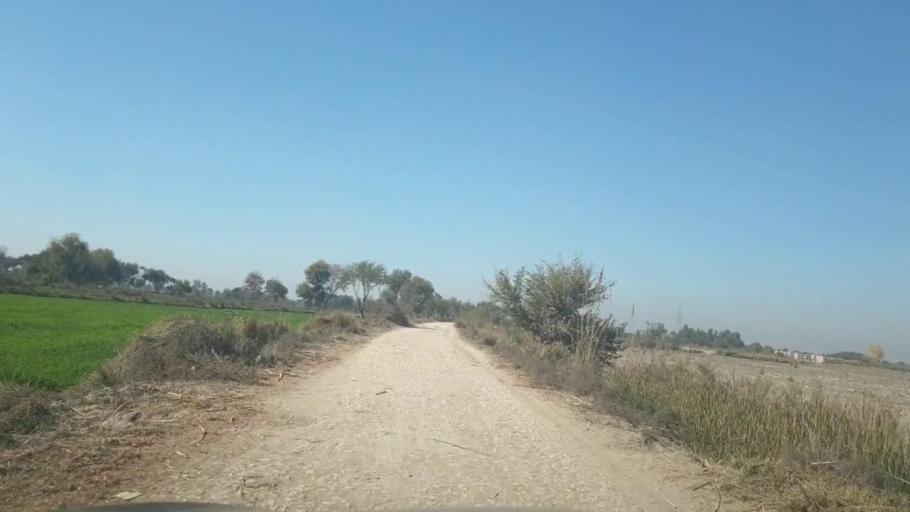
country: PK
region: Sindh
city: Adilpur
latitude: 27.8927
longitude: 69.2814
